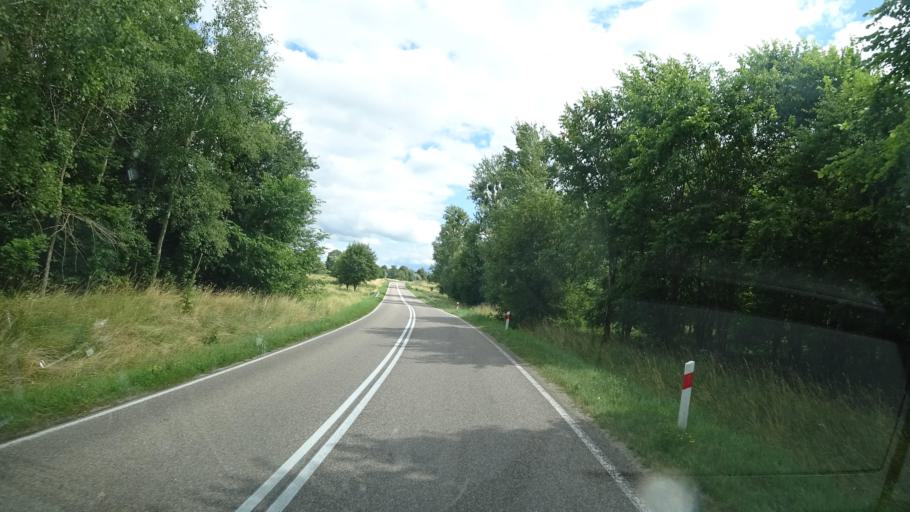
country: PL
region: Warmian-Masurian Voivodeship
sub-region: Powiat goldapski
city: Banie Mazurskie
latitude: 54.2112
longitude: 22.1773
